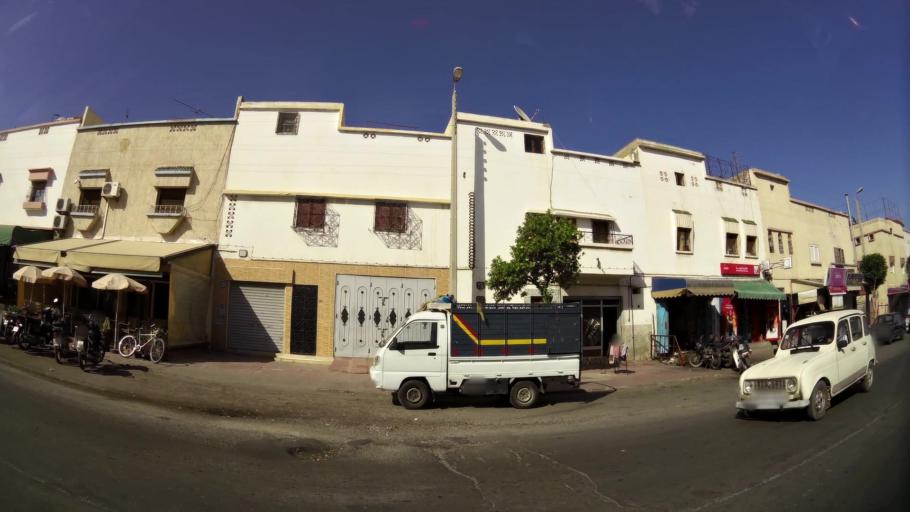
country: MA
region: Oued ed Dahab-Lagouira
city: Dakhla
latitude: 30.4232
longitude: -9.5643
